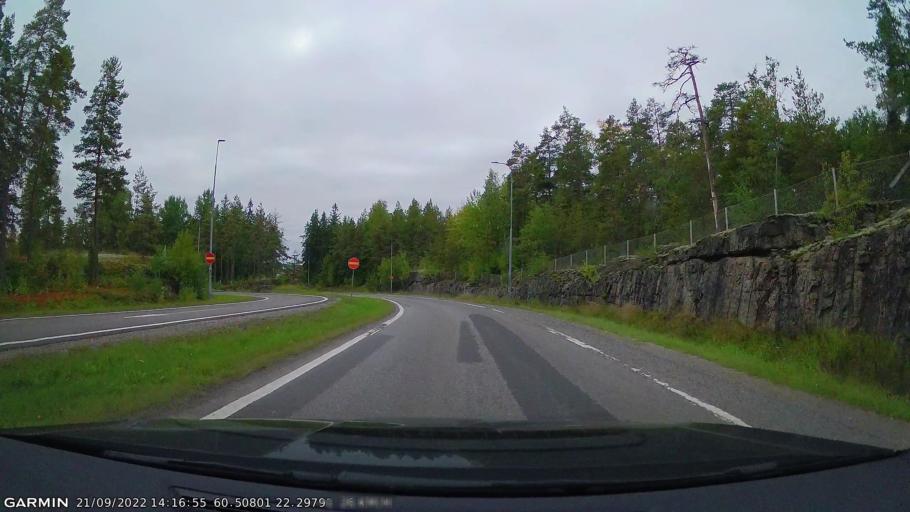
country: FI
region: Varsinais-Suomi
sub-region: Turku
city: Turku
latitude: 60.5078
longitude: 22.2970
